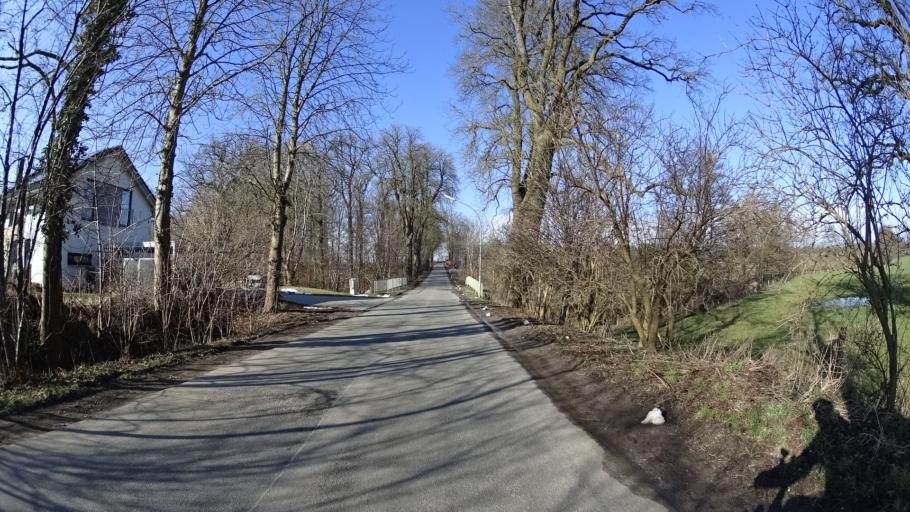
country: DE
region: Schleswig-Holstein
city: Schellhorn
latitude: 54.2511
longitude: 10.3237
